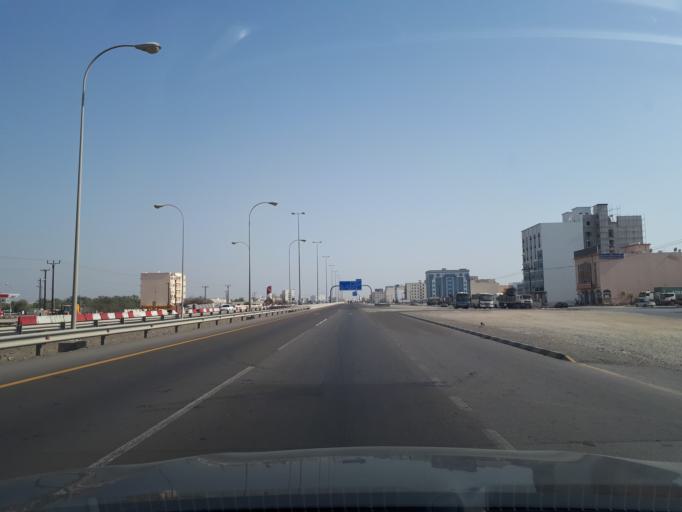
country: OM
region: Al Batinah
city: Al Liwa'
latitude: 24.4412
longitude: 56.6077
